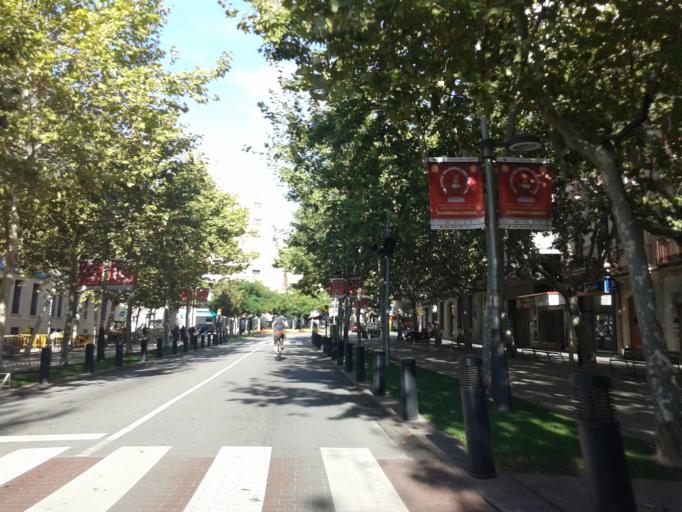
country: ES
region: Catalonia
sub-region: Provincia de Barcelona
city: Vilafranca del Penedes
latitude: 41.3453
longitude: 1.7002
